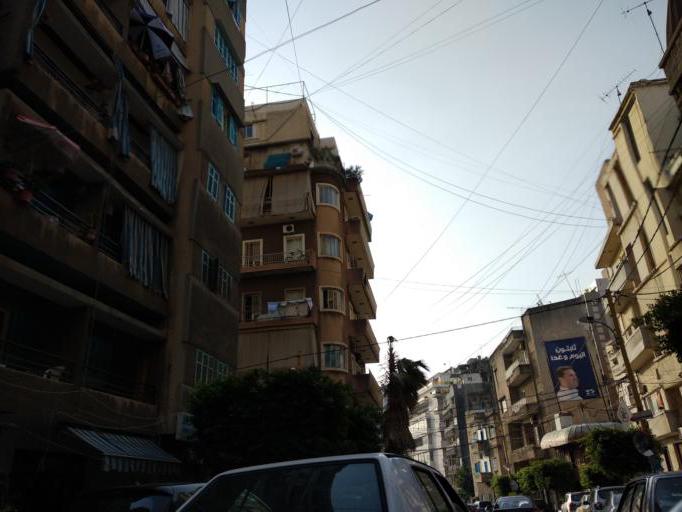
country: LB
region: Beyrouth
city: Beirut
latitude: 33.8871
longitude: 35.5265
